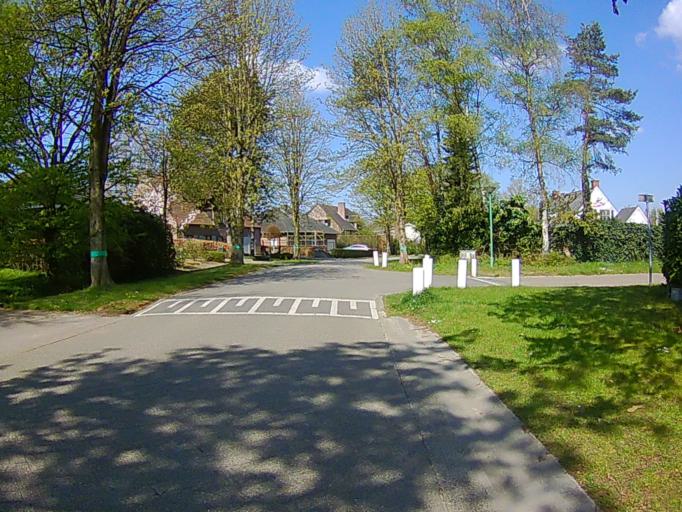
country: BE
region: Flanders
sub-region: Provincie Antwerpen
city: Schilde
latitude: 51.2280
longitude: 4.5838
